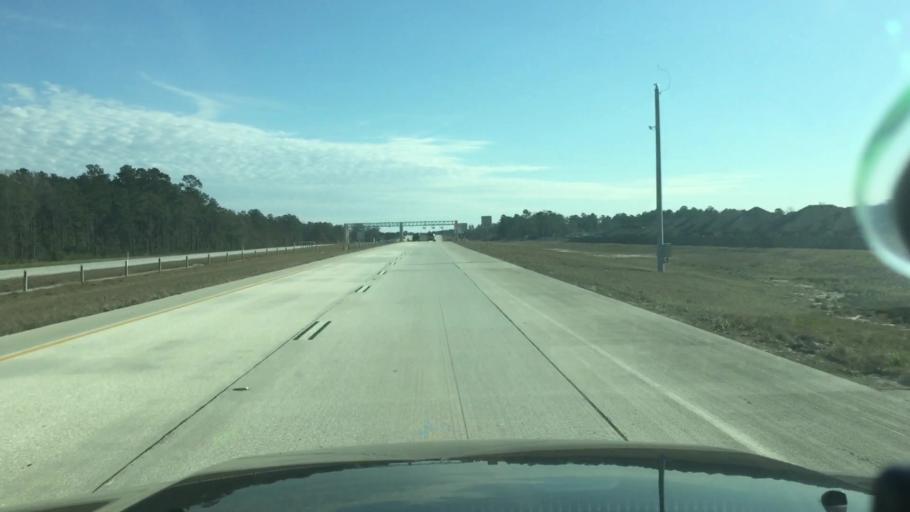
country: US
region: Texas
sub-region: Montgomery County
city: Porter Heights
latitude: 30.1376
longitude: -95.2819
